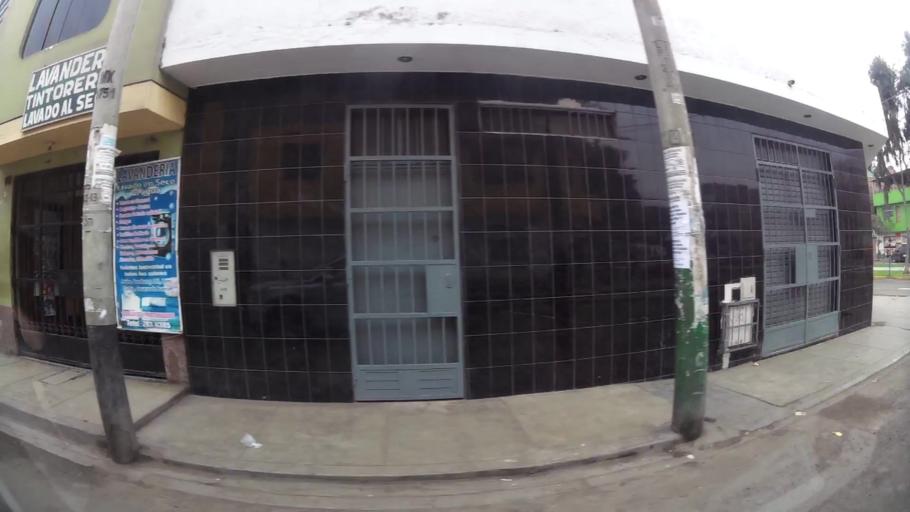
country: PE
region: Lima
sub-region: Lima
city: Surco
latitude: -12.1541
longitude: -76.9539
